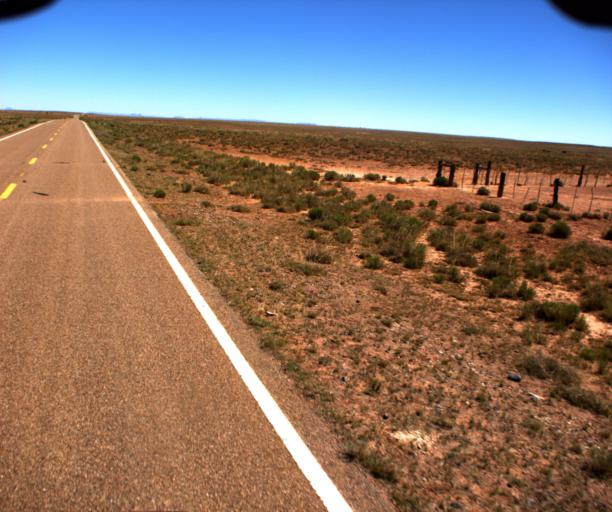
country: US
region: Arizona
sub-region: Navajo County
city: Winslow
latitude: 34.8383
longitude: -110.6714
